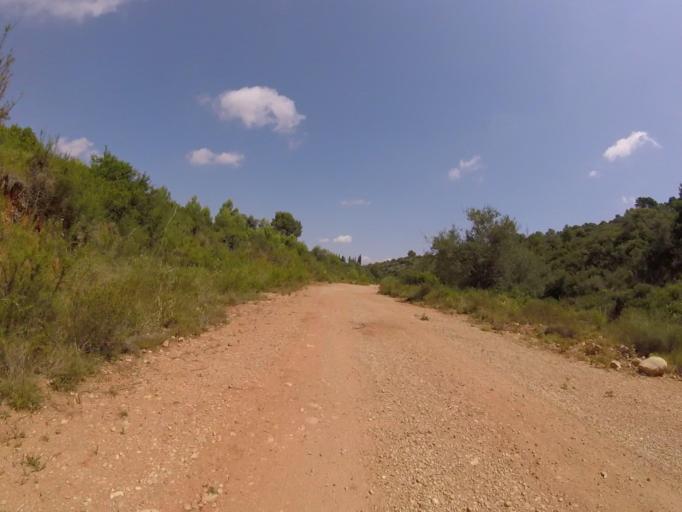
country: ES
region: Valencia
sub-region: Provincia de Castello
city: Torreblanca
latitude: 40.2078
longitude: 0.1393
